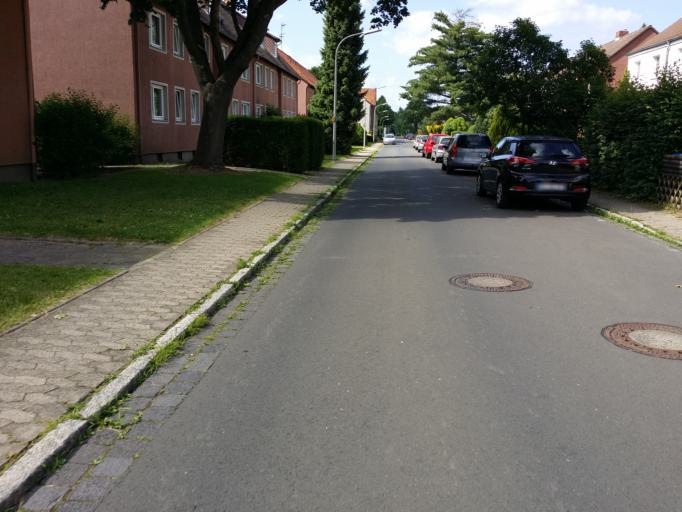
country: DE
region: Lower Saxony
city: Braunschweig
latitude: 52.2927
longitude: 10.5461
